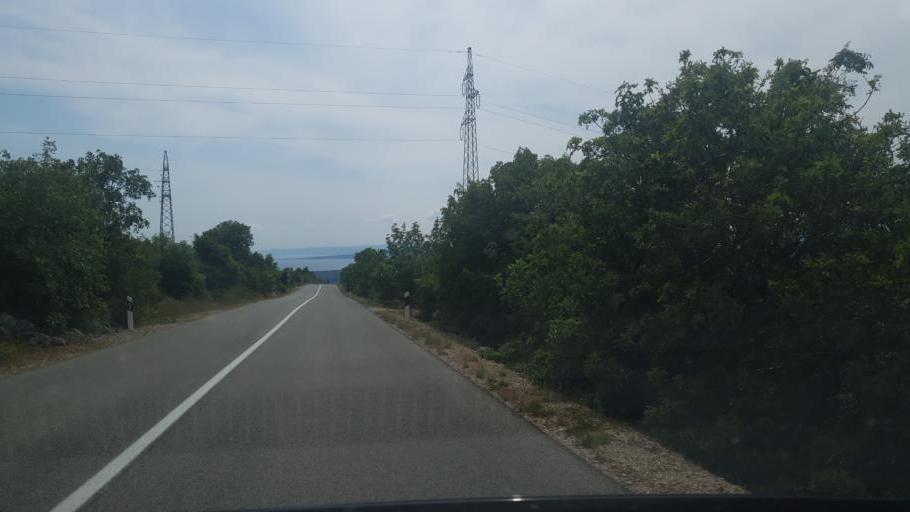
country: HR
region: Primorsko-Goranska
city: Punat
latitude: 45.0465
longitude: 14.6414
